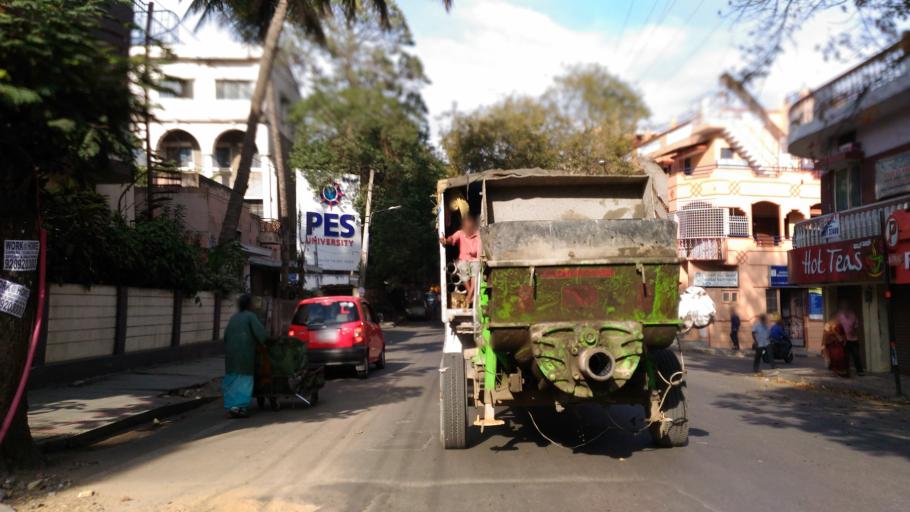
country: IN
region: Karnataka
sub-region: Bangalore Urban
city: Bangalore
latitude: 12.9418
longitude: 77.5553
